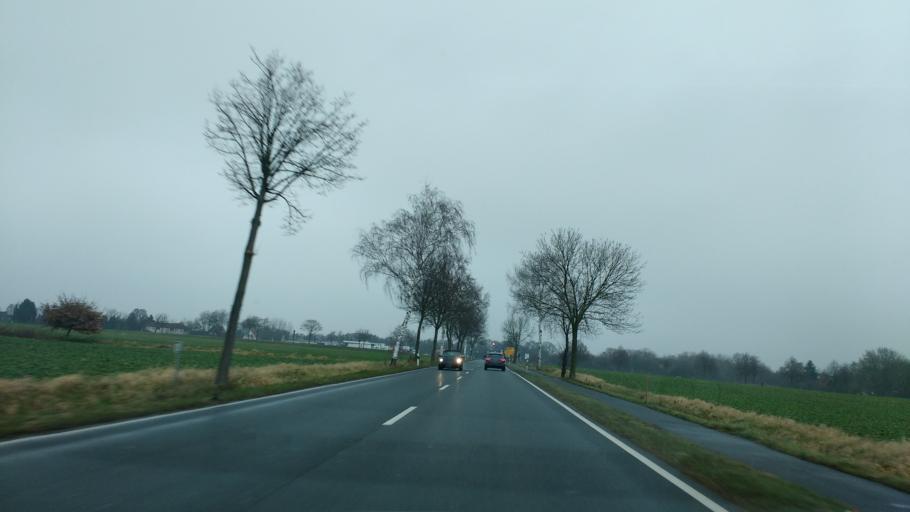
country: DE
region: Lower Saxony
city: Garbsen-Mitte
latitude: 52.4359
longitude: 9.5862
